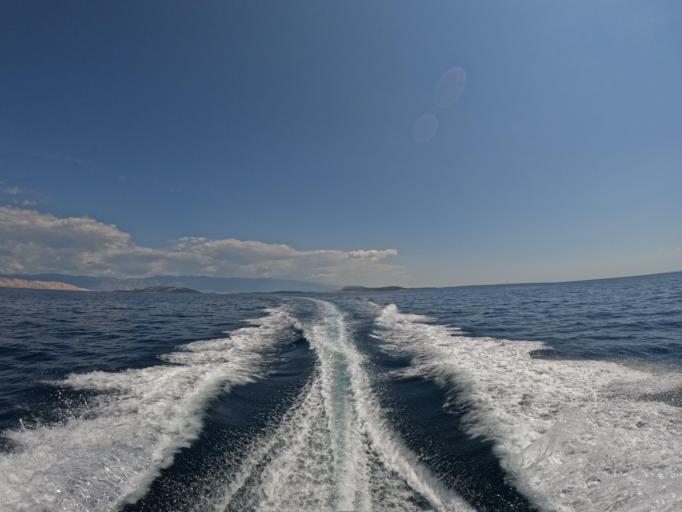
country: HR
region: Primorsko-Goranska
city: Lopar
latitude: 44.8855
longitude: 14.6417
